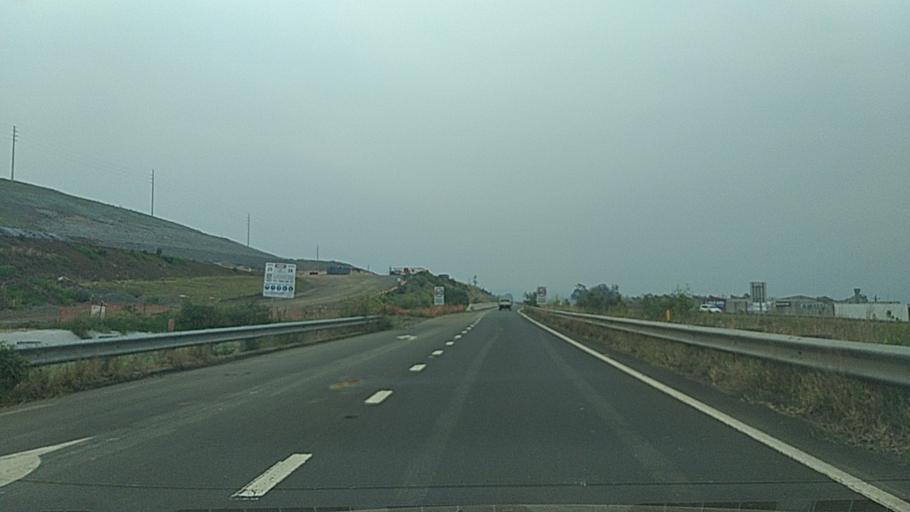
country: AU
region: New South Wales
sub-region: Shellharbour
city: Albion Park Rail
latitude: -34.5750
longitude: 150.8190
